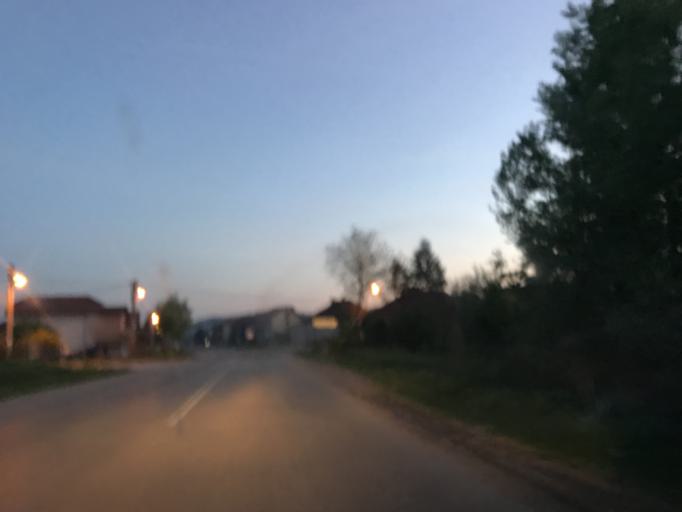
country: RS
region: Central Serbia
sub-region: Zajecarski Okrug
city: Zajecar
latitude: 43.9083
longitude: 22.2956
